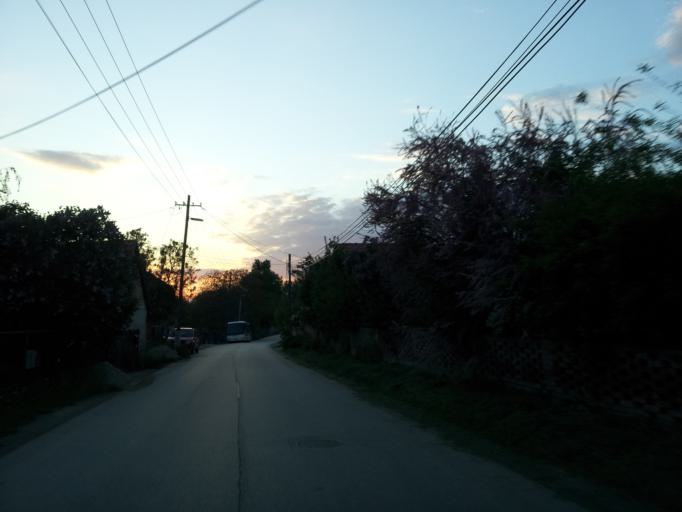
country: HU
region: Pest
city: Perbal
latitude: 47.6228
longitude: 18.7726
